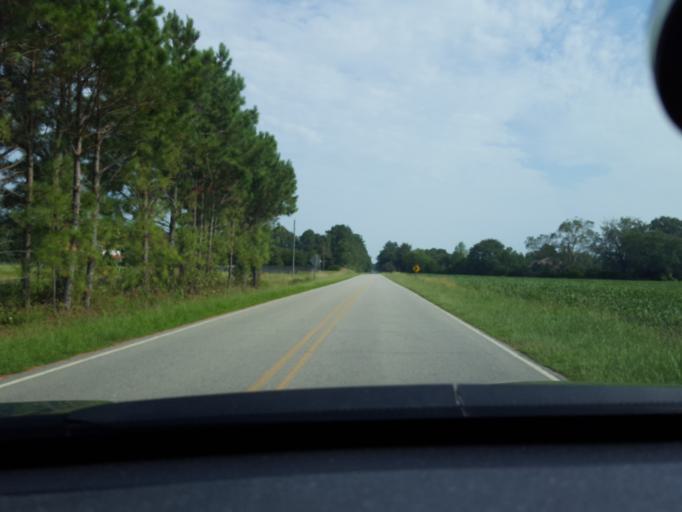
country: US
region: North Carolina
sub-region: Washington County
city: Plymouth
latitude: 35.8796
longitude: -76.7118
